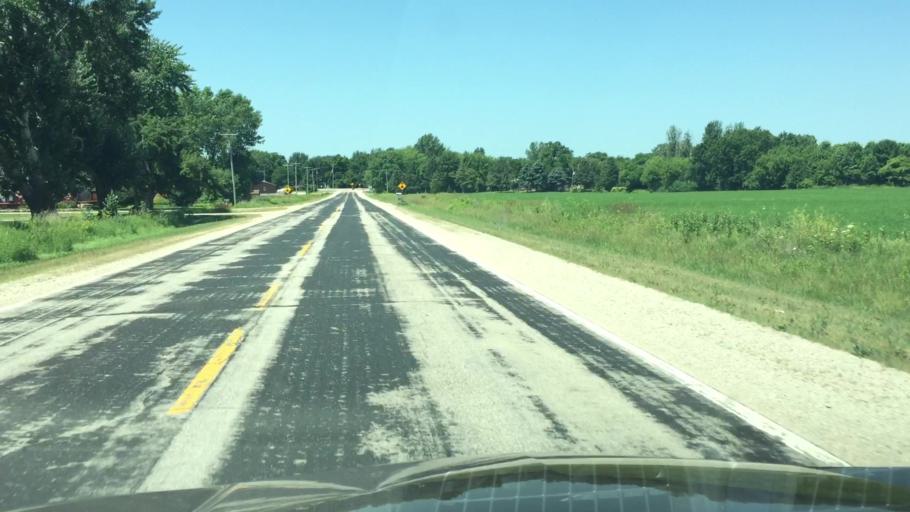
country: US
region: Wisconsin
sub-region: Fond du Lac County
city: Saint Peter
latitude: 43.9696
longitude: -88.3027
